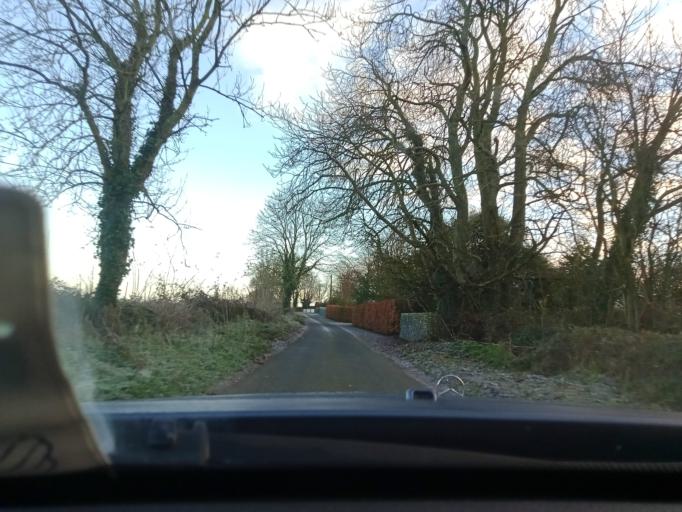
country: IE
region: Leinster
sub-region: County Carlow
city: Bagenalstown
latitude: 52.6375
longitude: -7.0347
